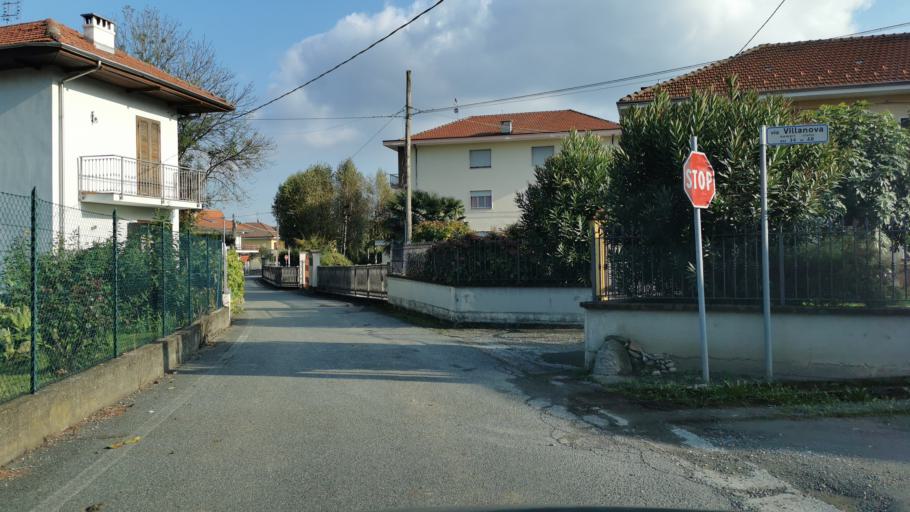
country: IT
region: Piedmont
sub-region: Provincia di Torino
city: Cafasse
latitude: 45.2452
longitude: 7.5206
